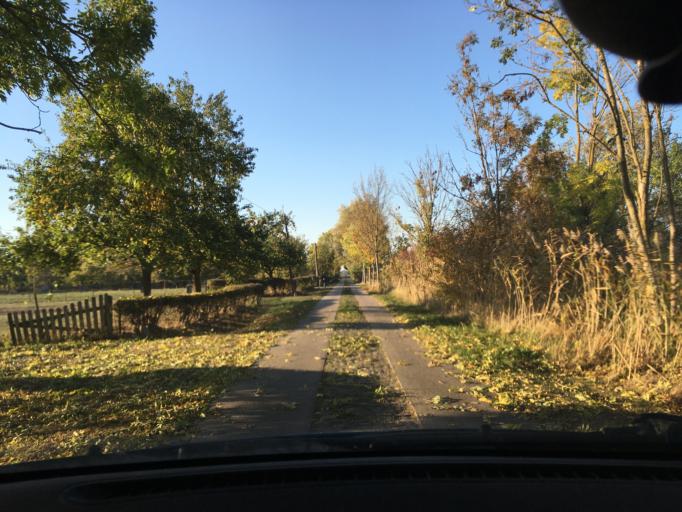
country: DE
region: Lower Saxony
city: Bleckede
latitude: 53.2868
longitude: 10.8065
